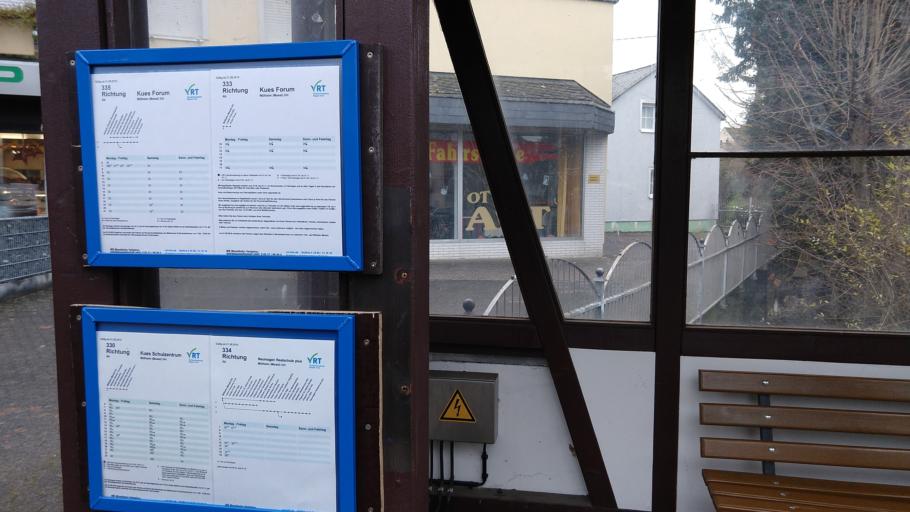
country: DE
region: Rheinland-Pfalz
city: Lieser
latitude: 49.9122
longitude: 7.0104
